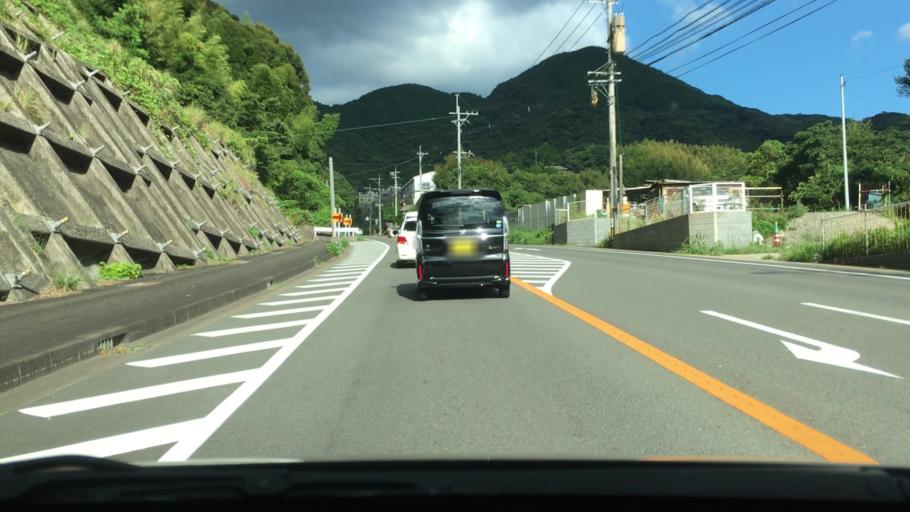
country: JP
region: Nagasaki
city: Togitsu
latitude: 32.8174
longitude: 129.8046
